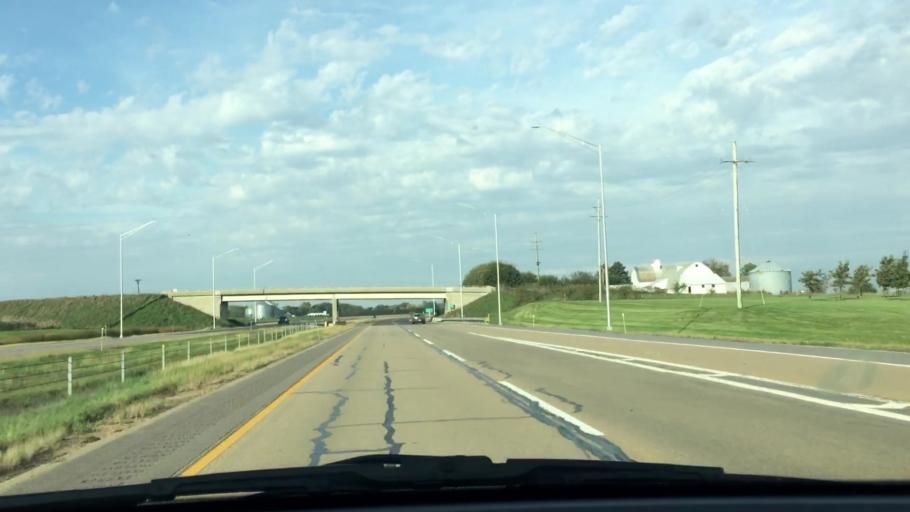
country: US
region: Illinois
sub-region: Lee County
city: Dixon
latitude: 41.8231
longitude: -89.4321
